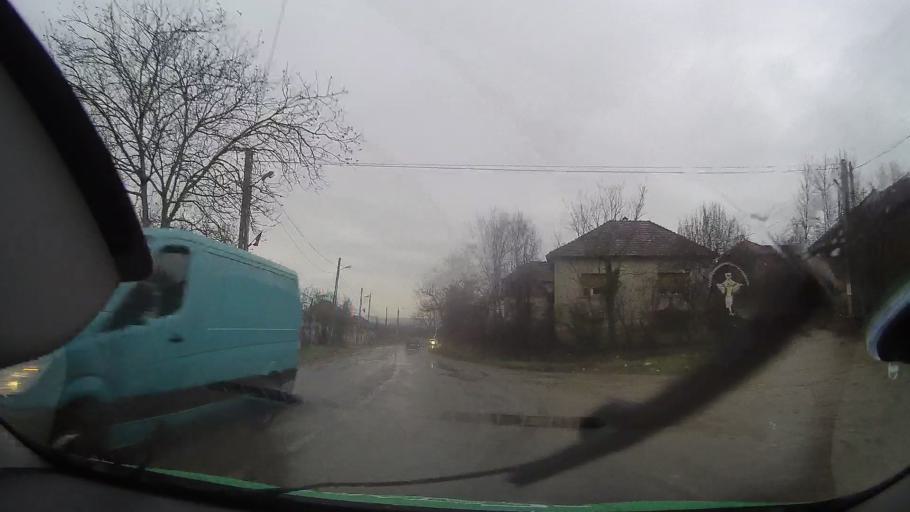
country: RO
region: Bihor
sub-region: Comuna Sambata
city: Sambata
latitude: 46.7732
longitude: 22.1885
